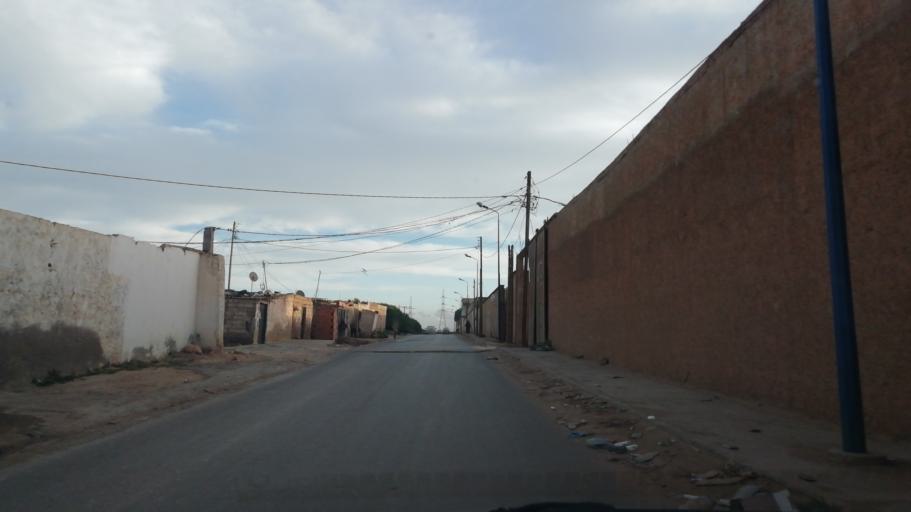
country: DZ
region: Oran
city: Es Senia
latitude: 35.6827
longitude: -0.5867
